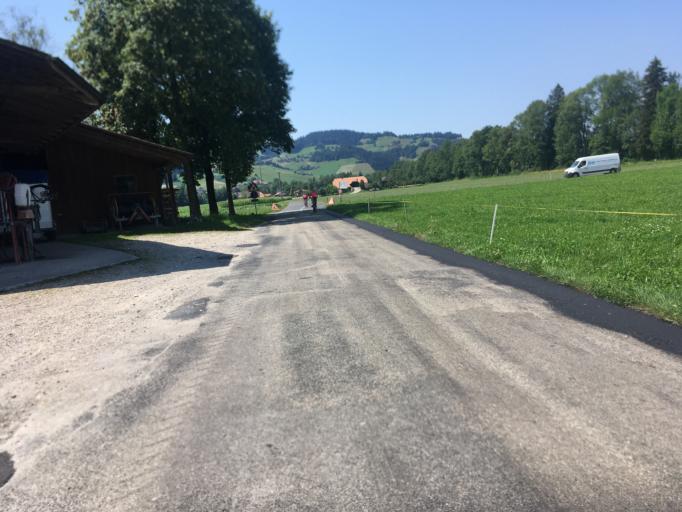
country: CH
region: Bern
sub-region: Emmental District
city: Lauperswil
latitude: 46.9458
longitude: 7.7596
